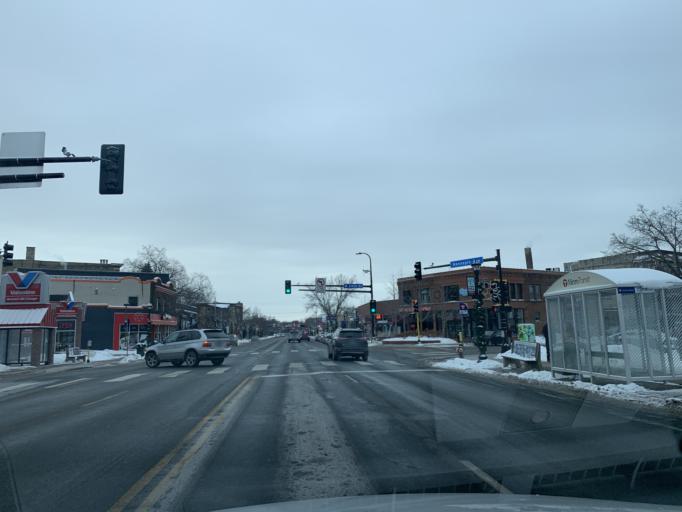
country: US
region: Minnesota
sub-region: Hennepin County
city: Minneapolis
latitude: 44.9594
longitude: -93.2939
